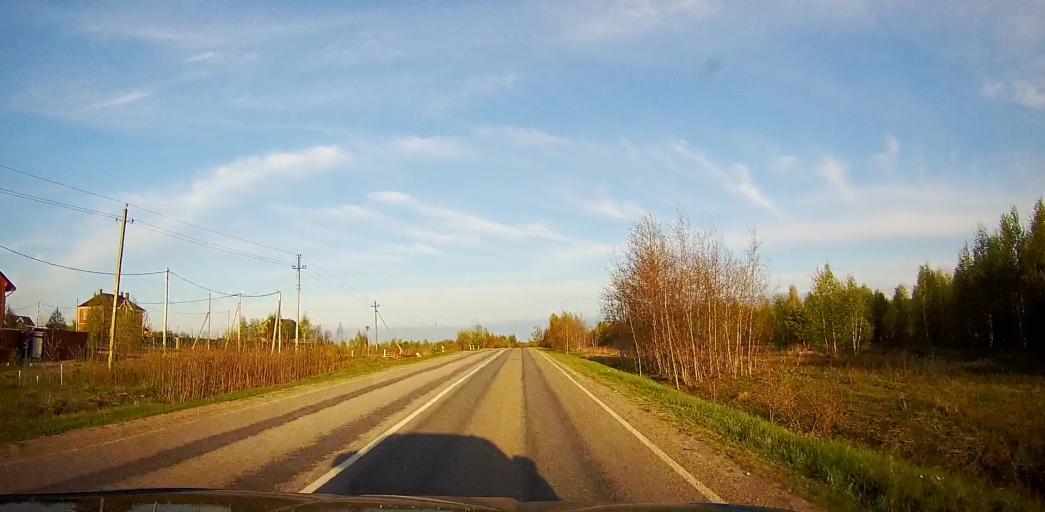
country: RU
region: Moskovskaya
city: Meshcherino
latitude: 55.2492
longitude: 38.2923
